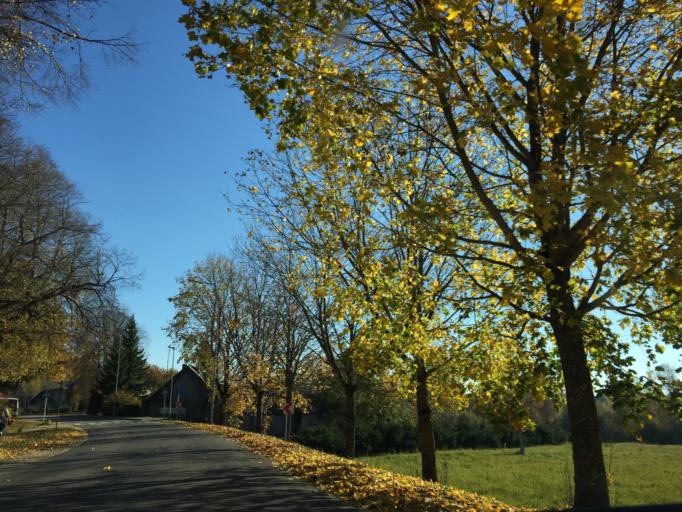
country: LT
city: Plateliai
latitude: 56.0272
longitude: 21.8090
